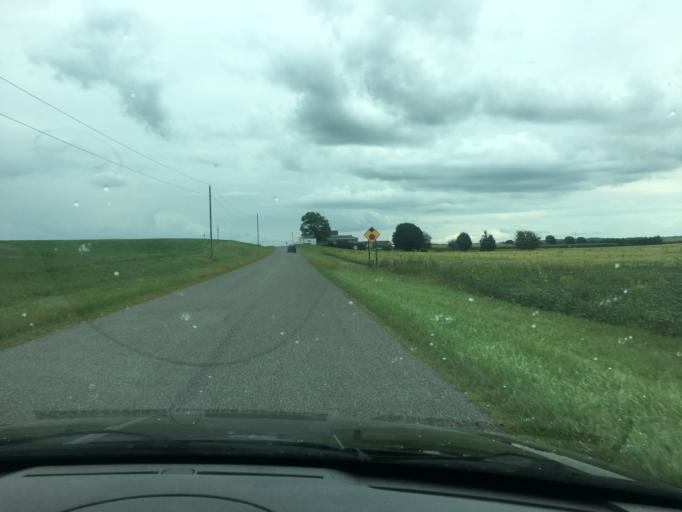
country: US
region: Ohio
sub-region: Logan County
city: West Liberty
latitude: 40.2109
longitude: -83.7047
